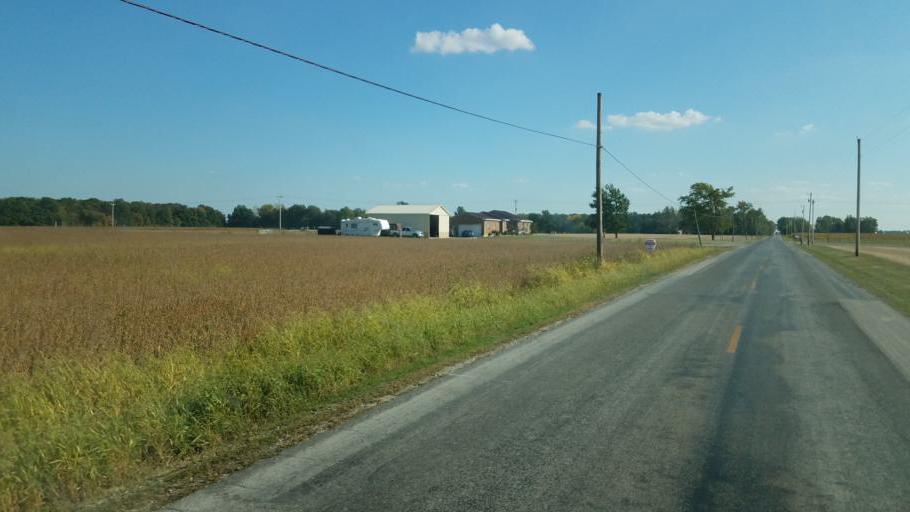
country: US
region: Ohio
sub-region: Union County
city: Richwood
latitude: 40.5485
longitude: -83.3898
